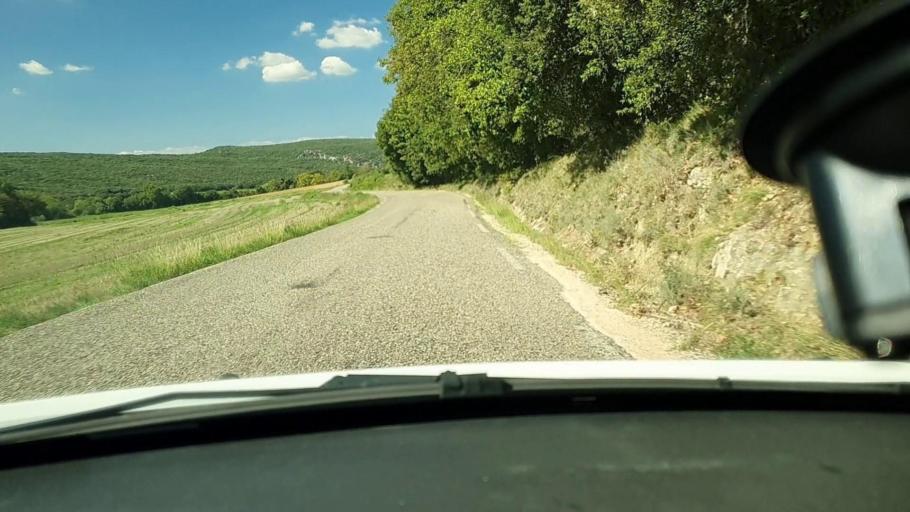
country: FR
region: Languedoc-Roussillon
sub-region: Departement du Gard
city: Goudargues
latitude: 44.1386
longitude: 4.4583
